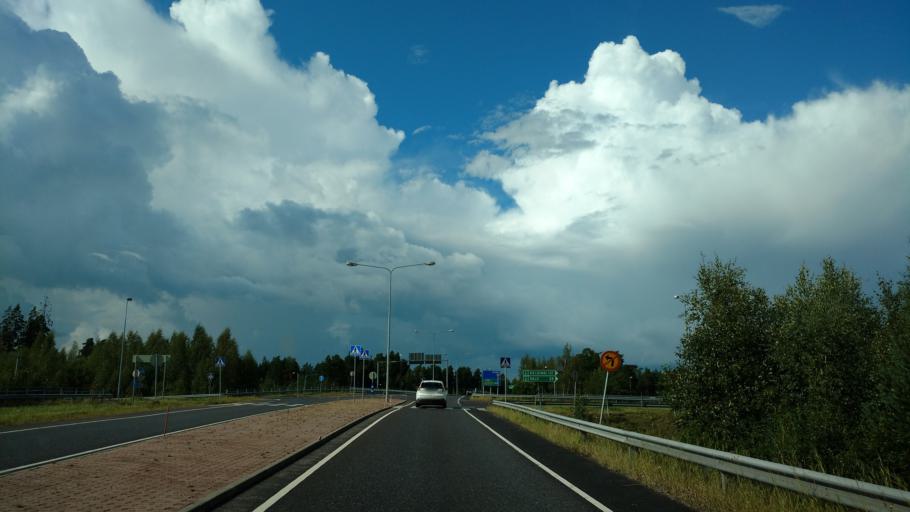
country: FI
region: Varsinais-Suomi
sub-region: Turku
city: Paimio
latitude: 60.4266
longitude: 22.7250
